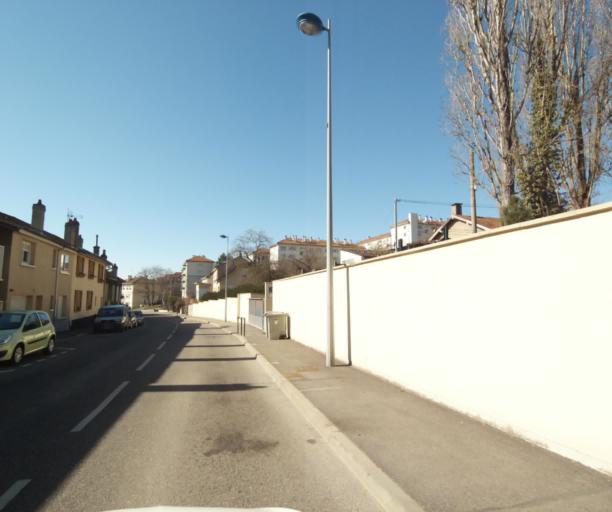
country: FR
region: Lorraine
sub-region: Departement de Meurthe-et-Moselle
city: Saint-Max
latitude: 48.7065
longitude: 6.2106
